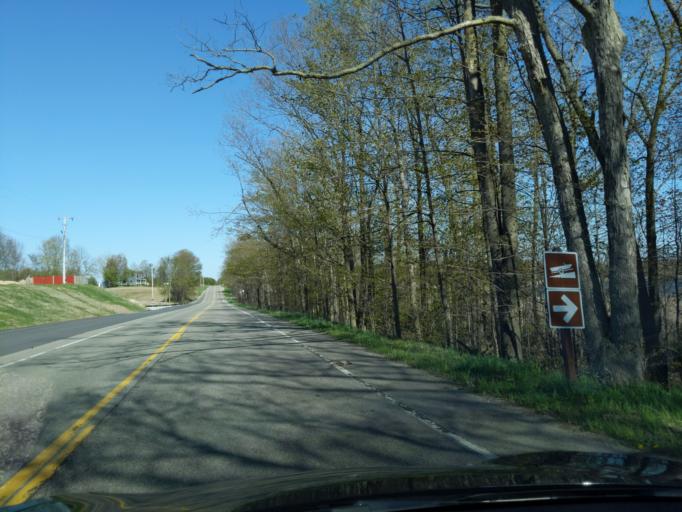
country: US
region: Michigan
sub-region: Kent County
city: Lowell
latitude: 42.8859
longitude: -85.3210
